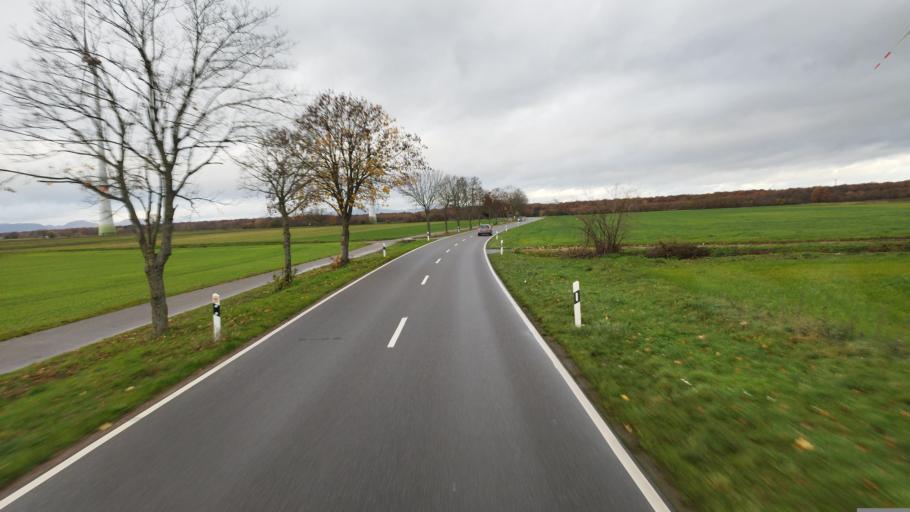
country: DE
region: Rheinland-Pfalz
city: Hatzenbuhl
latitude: 49.1186
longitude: 8.2381
